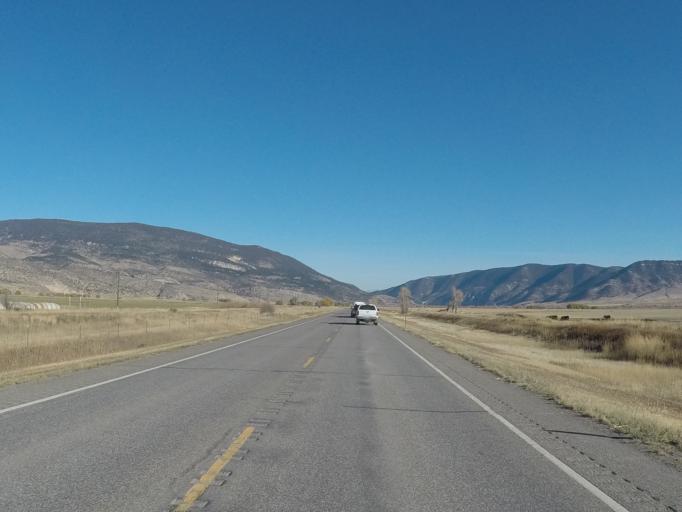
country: US
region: Montana
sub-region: Park County
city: Livingston
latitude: 45.5340
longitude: -110.6039
